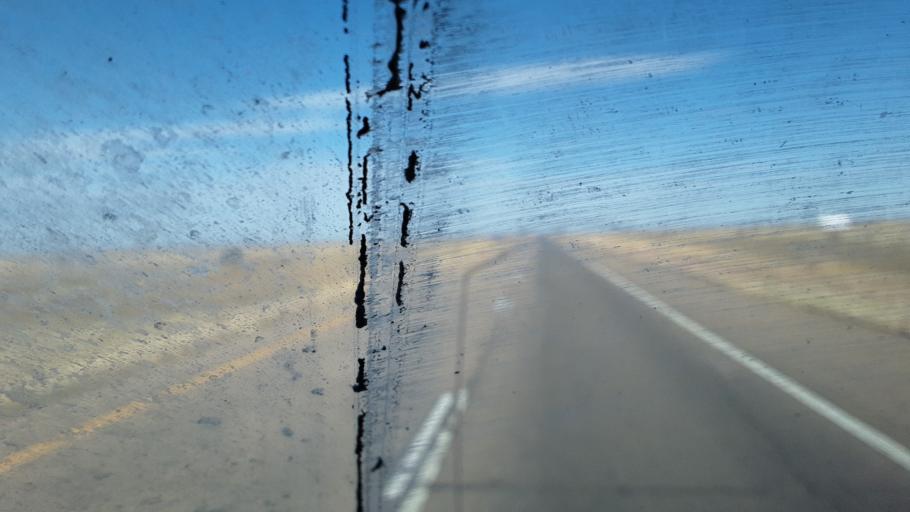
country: US
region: Colorado
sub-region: Weld County
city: Keenesburg
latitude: 40.1362
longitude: -104.4826
